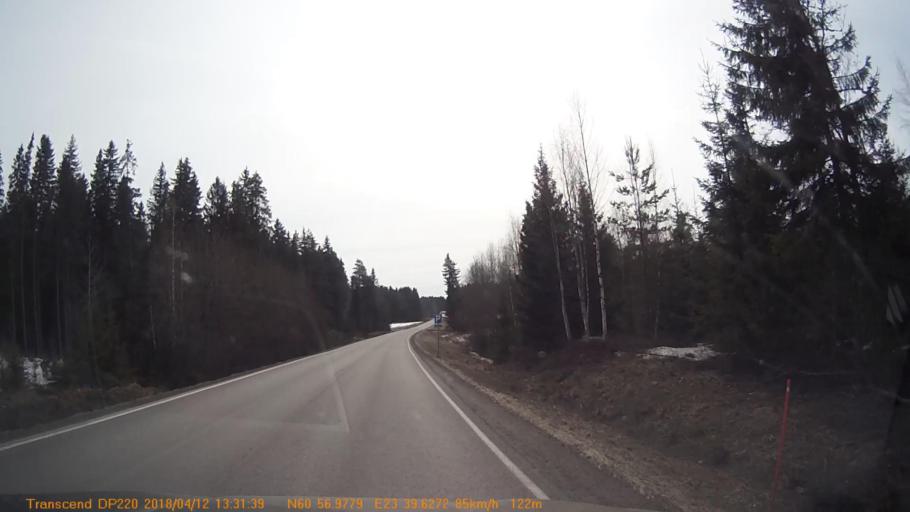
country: FI
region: Haeme
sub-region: Forssa
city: Forssa
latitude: 60.9495
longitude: 23.6604
